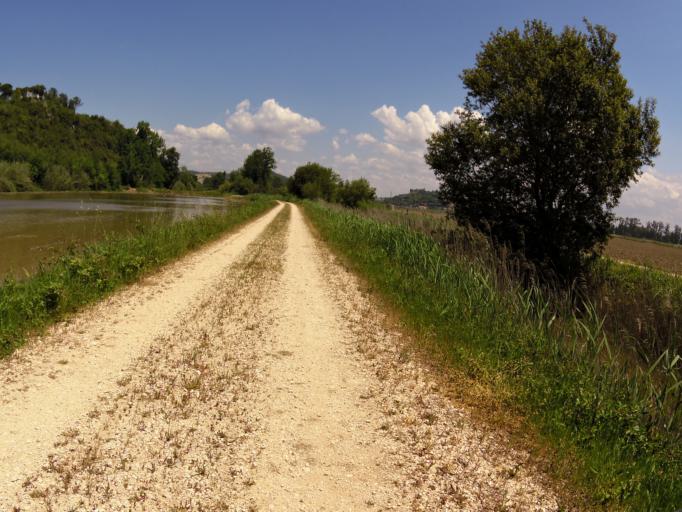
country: PT
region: Coimbra
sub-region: Montemor-O-Velho
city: Montemor-o-Velho
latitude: 40.1718
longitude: -8.7020
